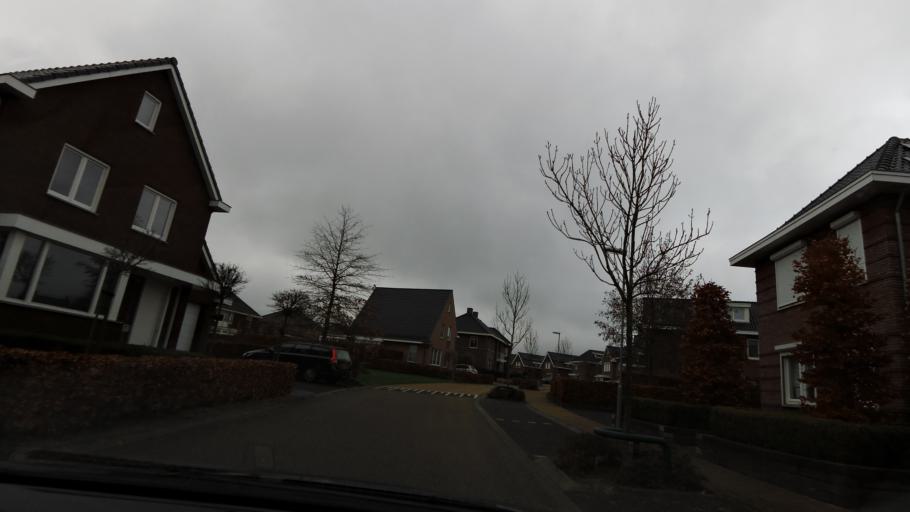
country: NL
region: Limburg
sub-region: Gemeente Simpelveld
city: Simpelveld
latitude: 50.8389
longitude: 5.9868
